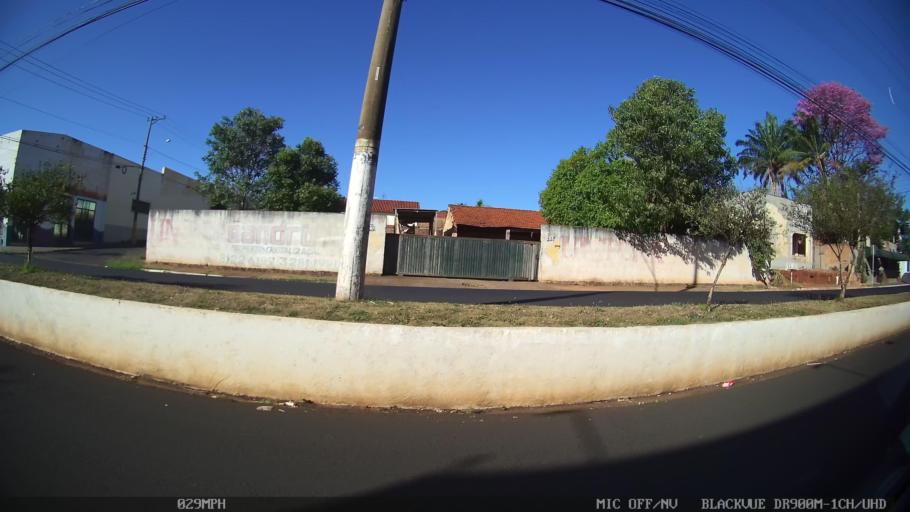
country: BR
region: Sao Paulo
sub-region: Olimpia
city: Olimpia
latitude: -20.7349
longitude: -48.9042
